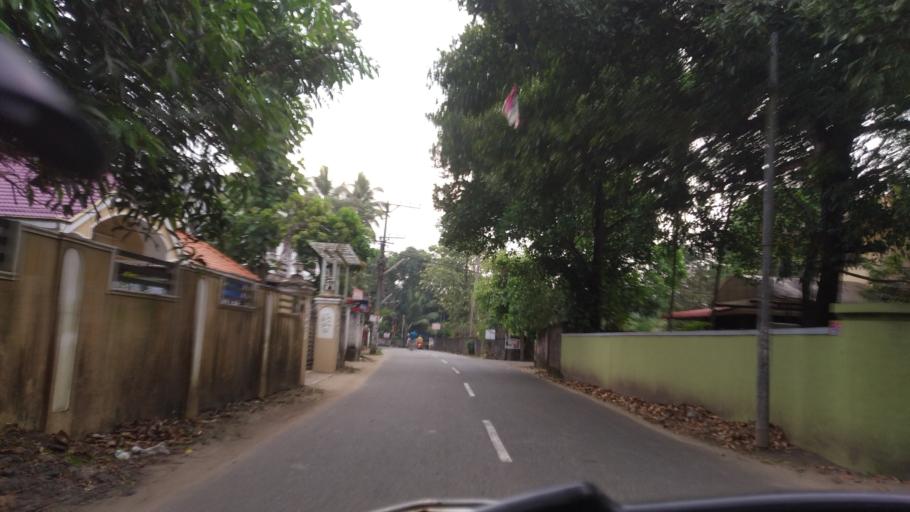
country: IN
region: Kerala
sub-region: Ernakulam
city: Elur
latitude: 10.1394
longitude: 76.2469
